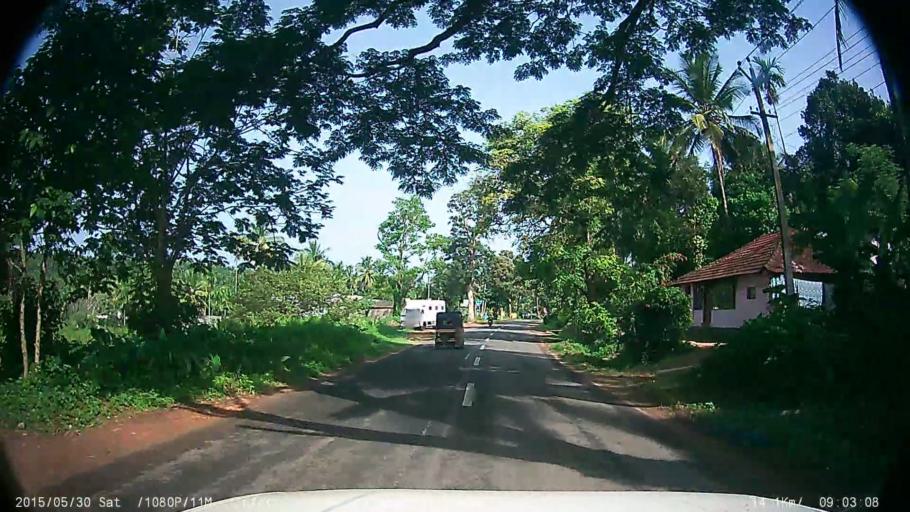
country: IN
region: Kerala
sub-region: Wayanad
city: Panamaram
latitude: 11.6674
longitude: 76.2726
